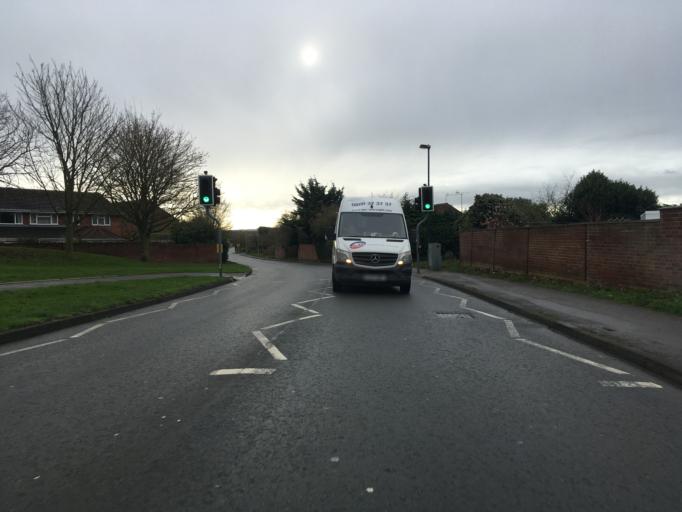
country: GB
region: England
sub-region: Worcestershire
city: Evesham
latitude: 52.0860
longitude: -1.9332
